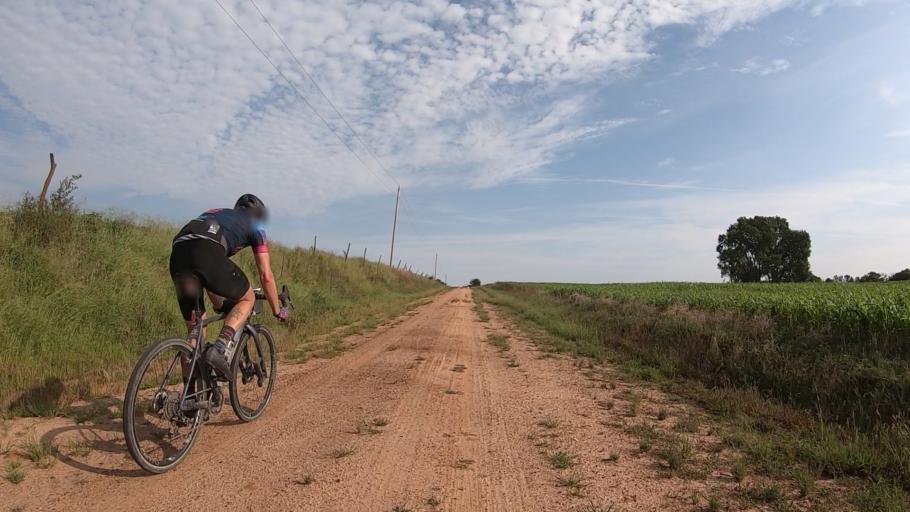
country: US
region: Kansas
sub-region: Washington County
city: Washington
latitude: 39.6732
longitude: -96.9471
